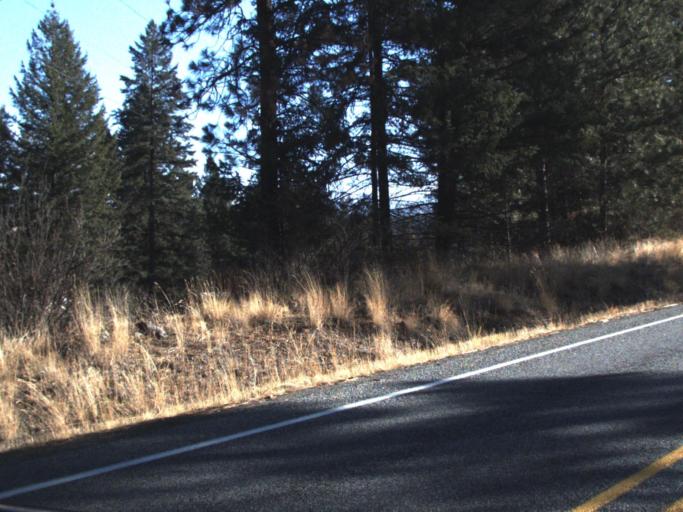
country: US
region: Washington
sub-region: Ferry County
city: Republic
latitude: 48.6511
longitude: -118.6805
